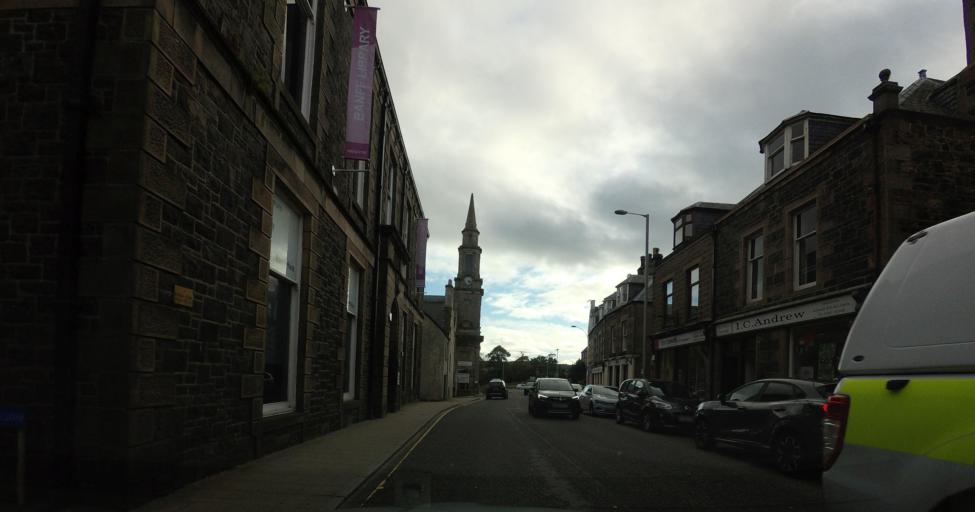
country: GB
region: Scotland
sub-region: Aberdeenshire
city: Banff
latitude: 57.6636
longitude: -2.5232
